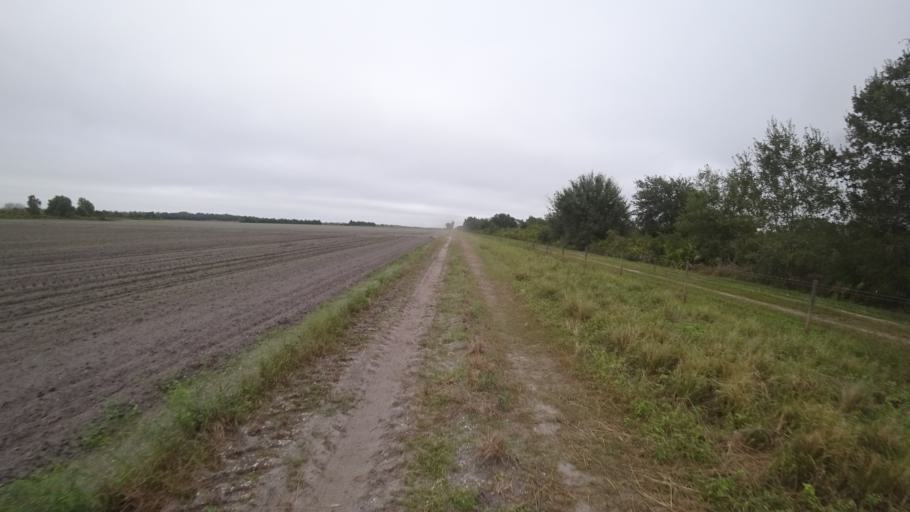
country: US
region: Florida
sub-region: Sarasota County
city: Warm Mineral Springs
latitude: 27.2772
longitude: -82.1346
